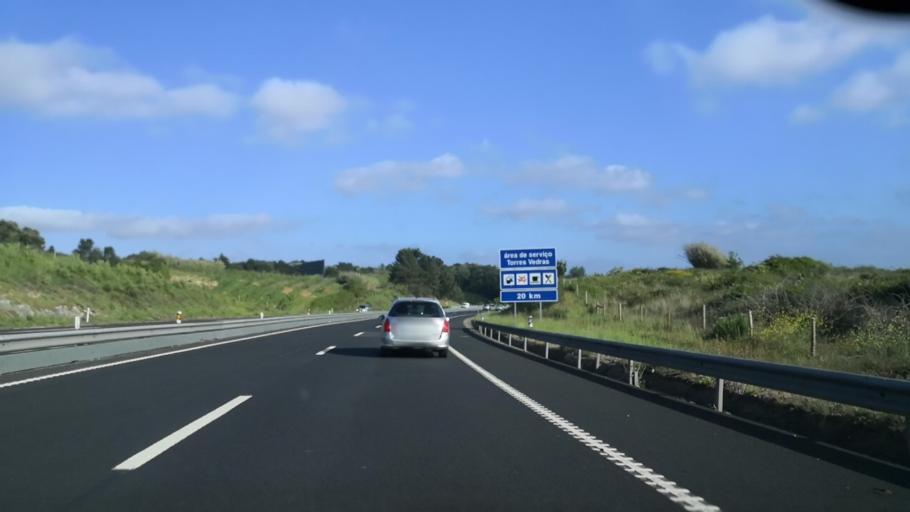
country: PT
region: Leiria
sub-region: Bombarral
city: Bombarral
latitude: 39.3098
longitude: -9.1713
